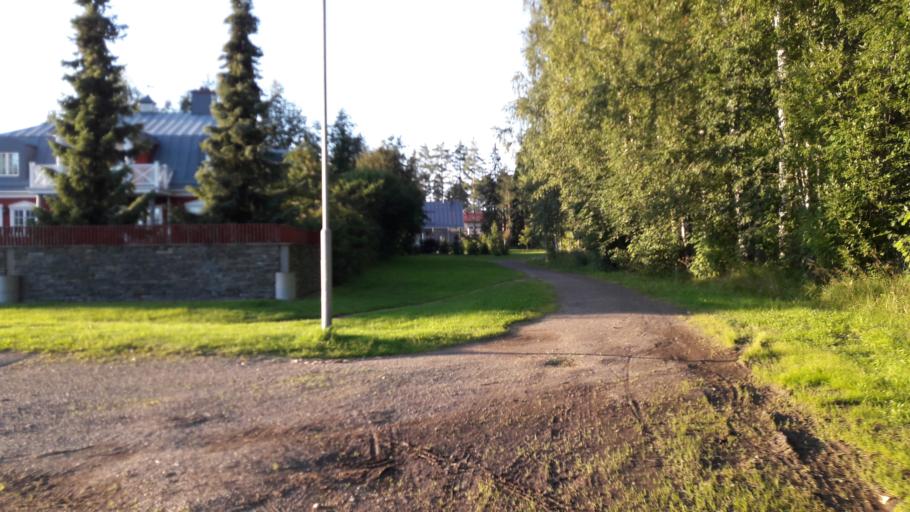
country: FI
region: North Karelia
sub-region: Joensuu
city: Joensuu
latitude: 62.6134
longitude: 29.7156
